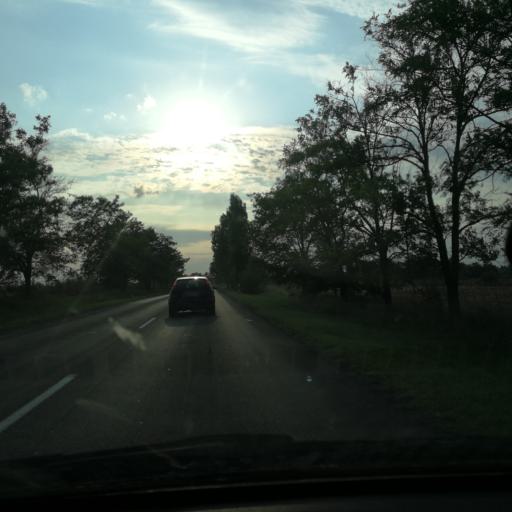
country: HU
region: Bacs-Kiskun
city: Palmonostora
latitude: 46.6974
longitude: 19.9237
